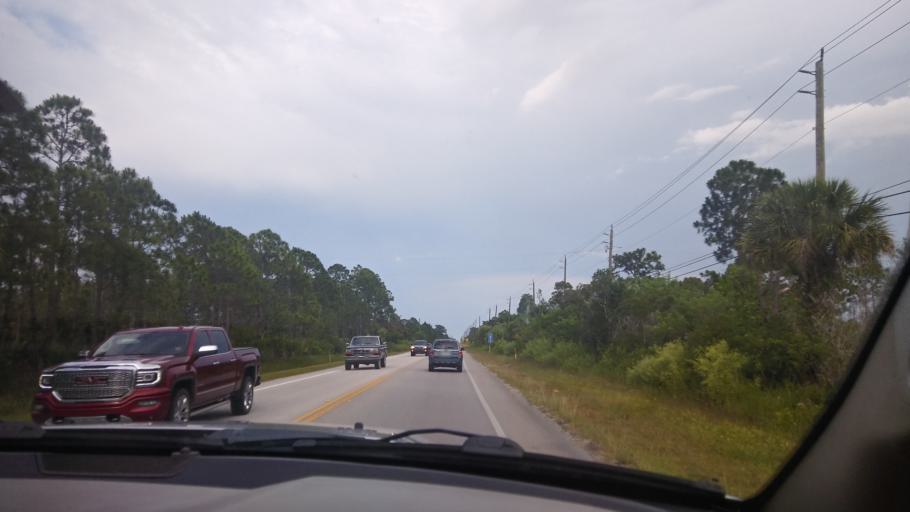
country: US
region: Florida
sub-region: Indian River County
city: Fellsmere
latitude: 27.7677
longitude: -80.5751
